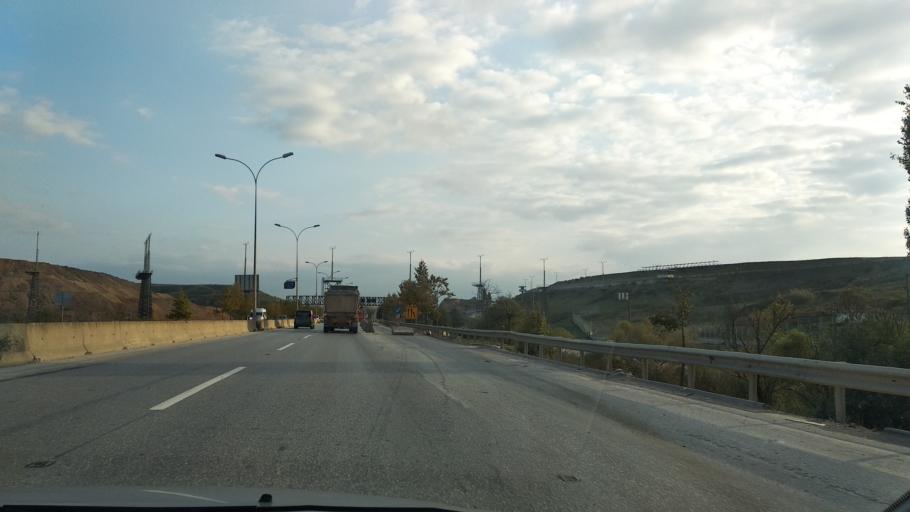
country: TR
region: Istanbul
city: Pendik
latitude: 40.9076
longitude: 29.3273
